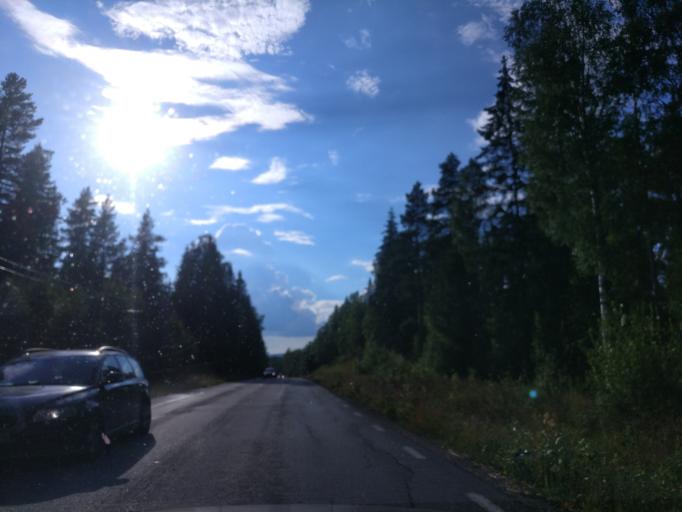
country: SE
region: Dalarna
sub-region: Ludvika Kommun
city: Grangesberg
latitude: 60.2671
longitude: 15.0264
